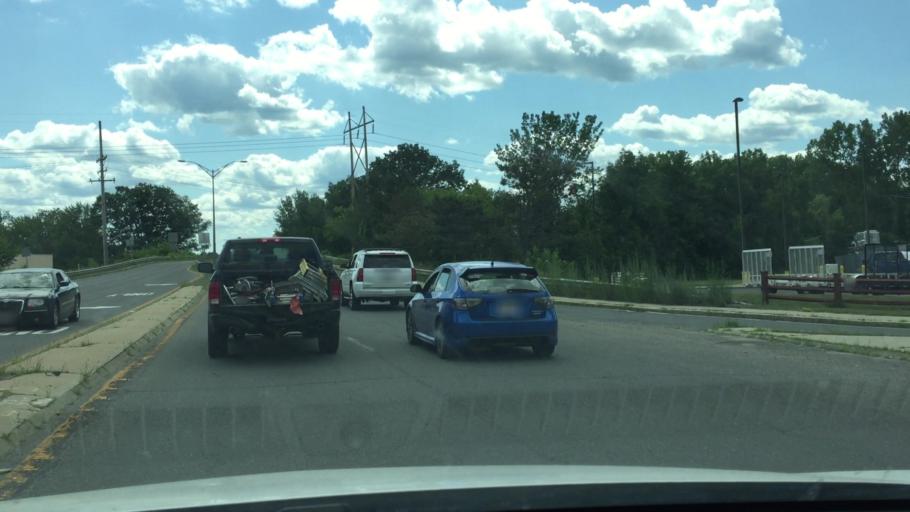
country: US
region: Massachusetts
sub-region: Berkshire County
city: Dalton
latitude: 42.4670
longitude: -73.2056
